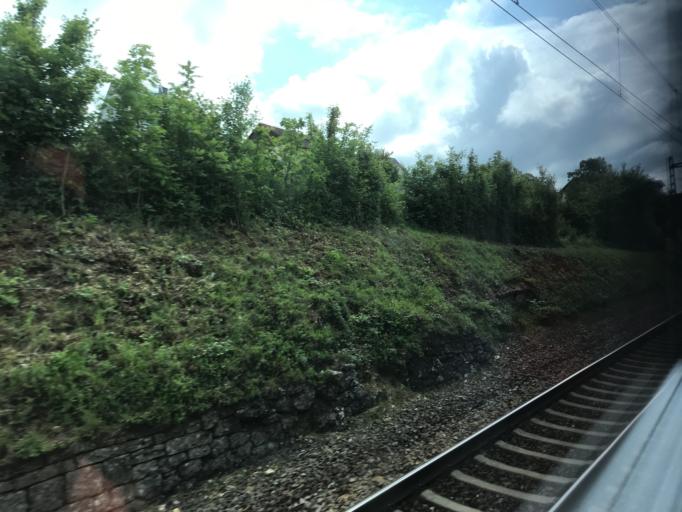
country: DE
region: Baden-Wuerttemberg
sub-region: Tuebingen Region
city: Lonsee
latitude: 48.5429
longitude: 9.9198
